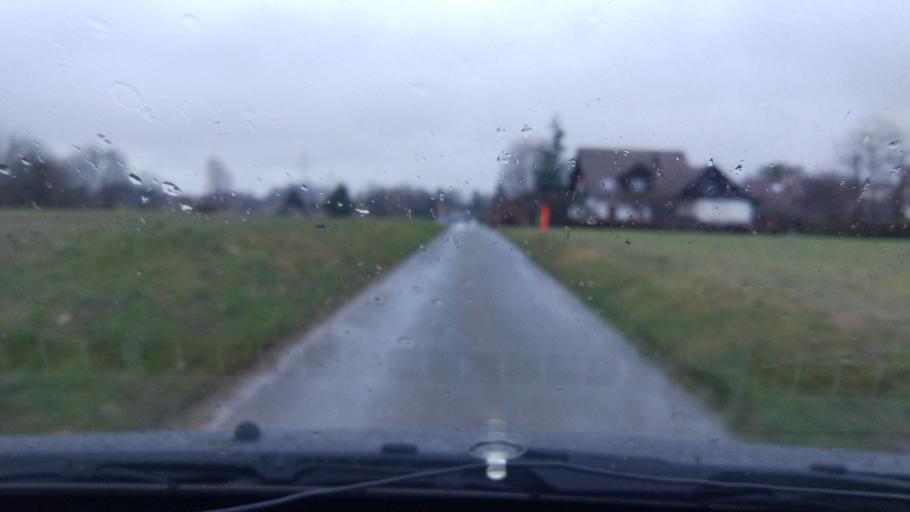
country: CH
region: Vaud
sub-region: Lausanne District
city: Le Mont-sur-Lausanne
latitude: 46.5575
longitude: 6.6259
